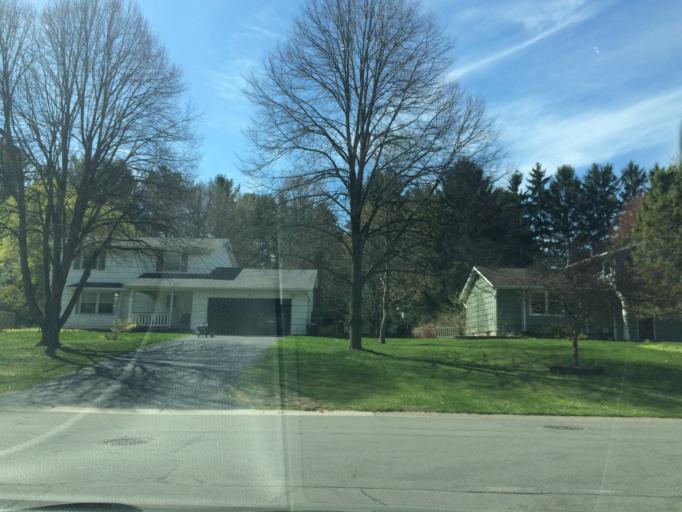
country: US
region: New York
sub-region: Monroe County
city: Fairport
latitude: 43.0894
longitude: -77.4678
